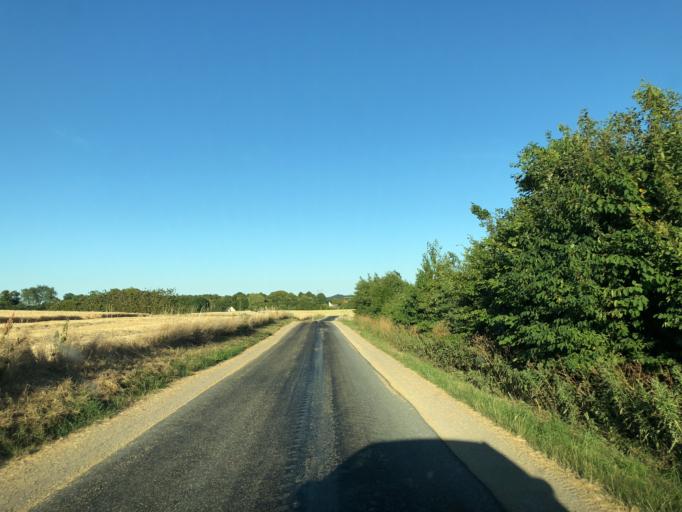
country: DK
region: Central Jutland
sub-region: Horsens Kommune
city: Horsens
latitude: 55.9212
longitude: 9.8874
